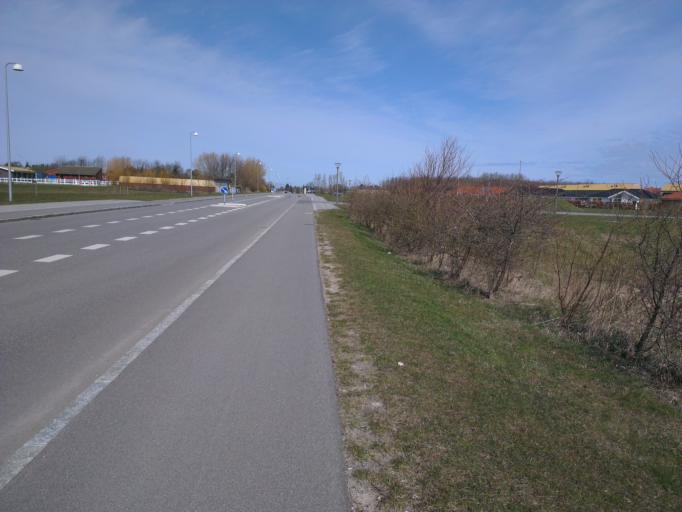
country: DK
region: Capital Region
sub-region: Frederikssund Kommune
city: Frederikssund
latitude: 55.8181
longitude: 12.0759
